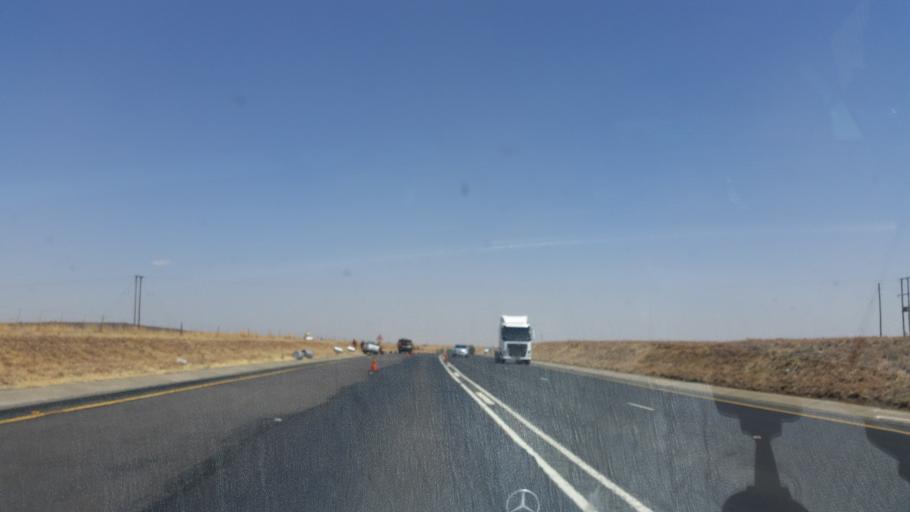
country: ZA
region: Orange Free State
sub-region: Lejweleputswa District Municipality
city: Brandfort
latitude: -28.8130
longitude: 26.6718
